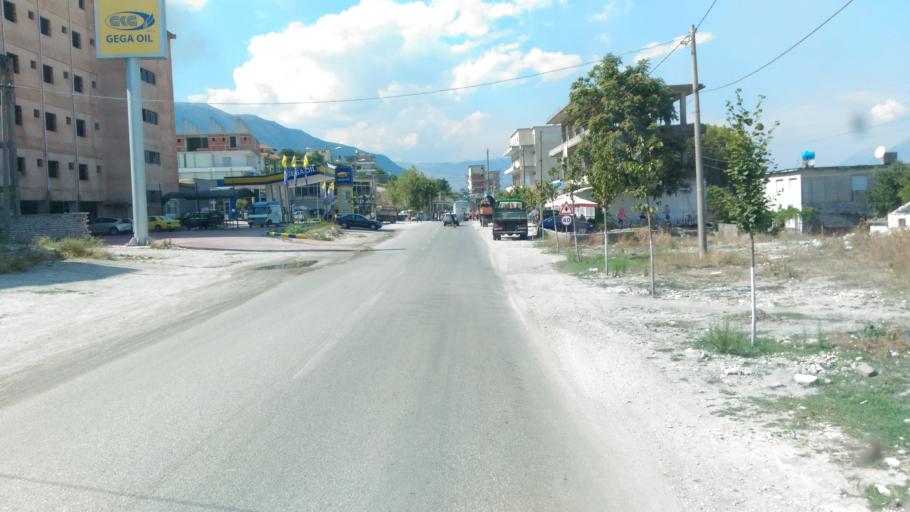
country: AL
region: Gjirokaster
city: Gjirokaster
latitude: 40.0733
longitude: 20.1561
